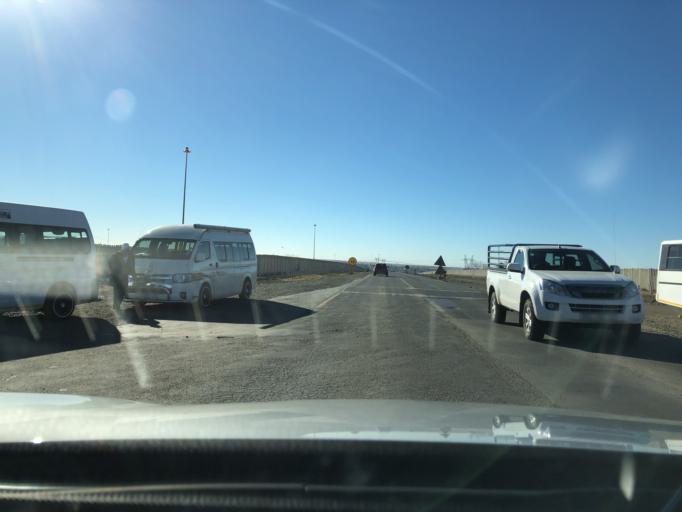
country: ZA
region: Mpumalanga
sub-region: Gert Sibande District Municipality
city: Standerton
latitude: -26.9408
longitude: 29.2075
